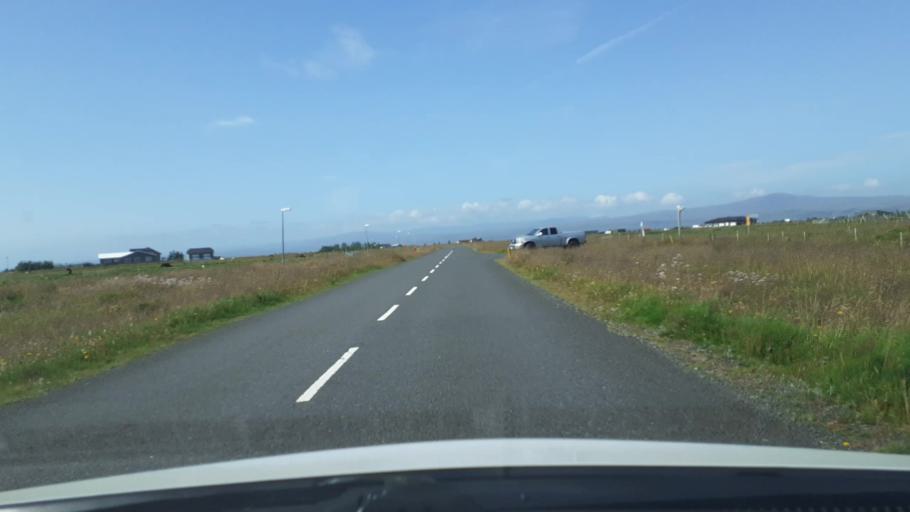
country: IS
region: South
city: Selfoss
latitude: 63.8934
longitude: -21.0817
